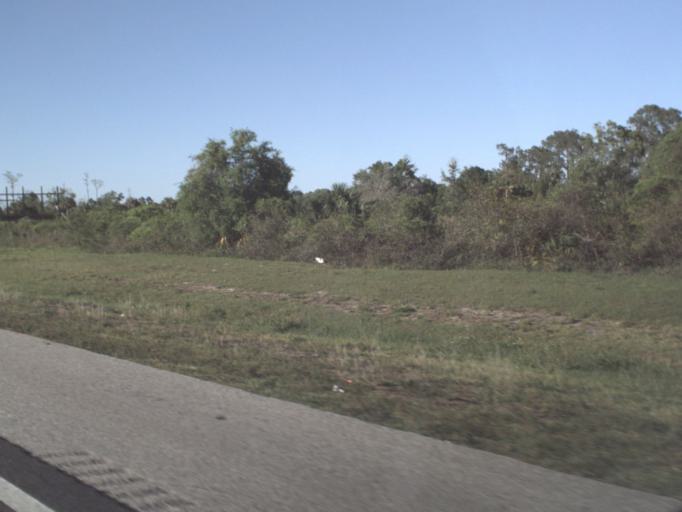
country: US
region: Florida
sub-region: Flagler County
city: Flagler Beach
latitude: 29.4212
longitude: -81.1626
